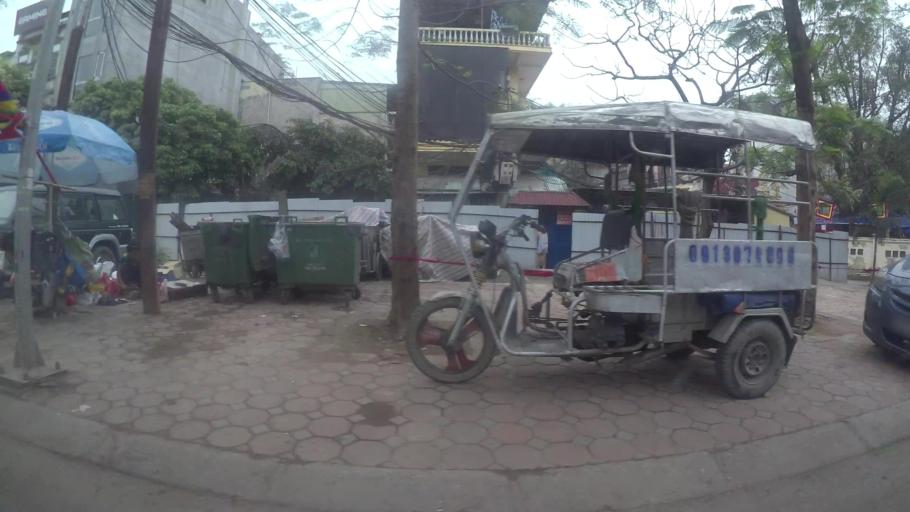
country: VN
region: Ha Noi
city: Dong Da
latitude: 21.0374
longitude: 105.8205
